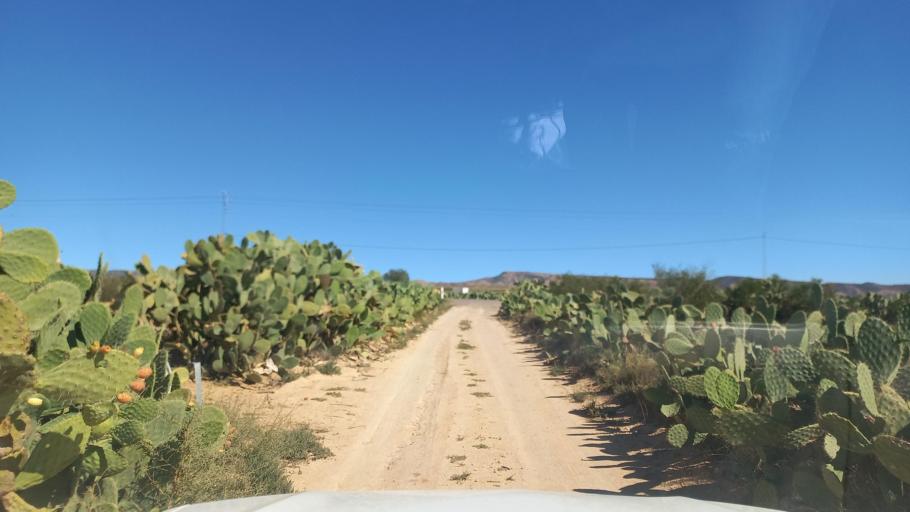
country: TN
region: Al Qasrayn
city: Sbiba
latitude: 35.3629
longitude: 9.0940
